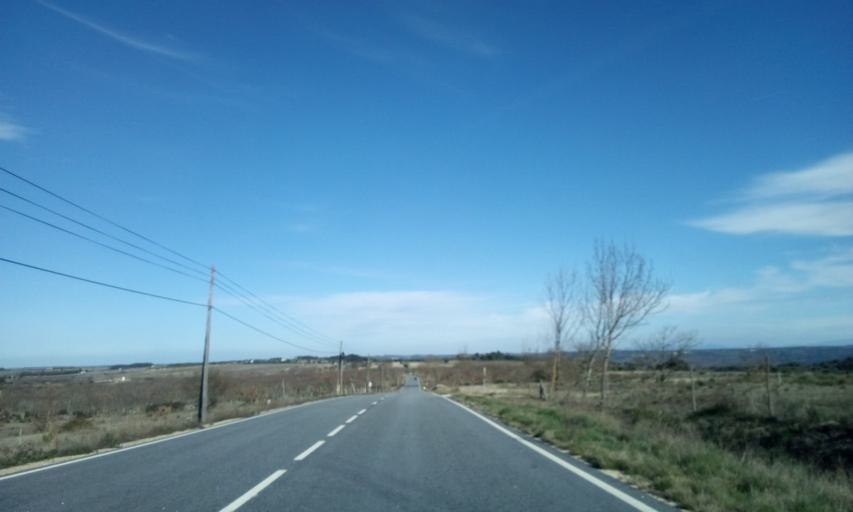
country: ES
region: Castille and Leon
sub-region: Provincia de Salamanca
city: Fuentes de Onoro
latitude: 40.5946
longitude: -6.9791
